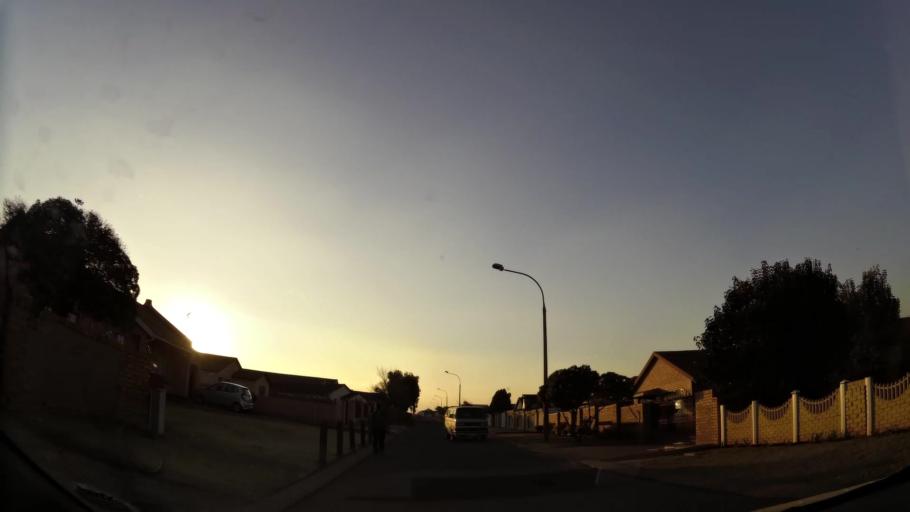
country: ZA
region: Gauteng
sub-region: West Rand District Municipality
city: Randfontein
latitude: -26.2095
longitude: 27.7057
